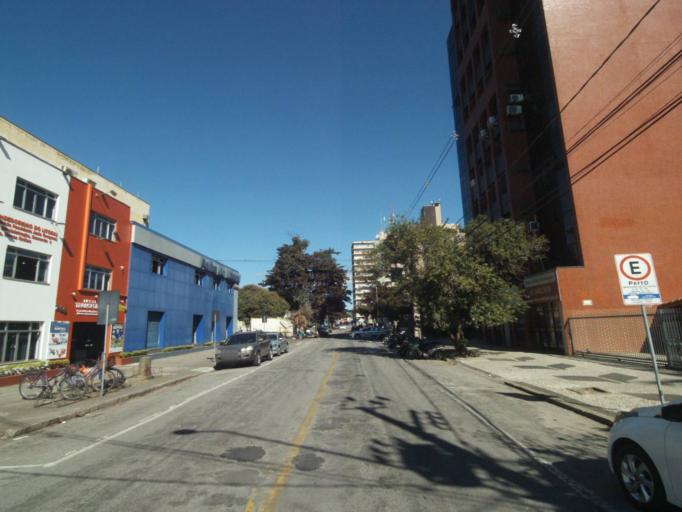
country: BR
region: Parana
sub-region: Paranagua
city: Paranagua
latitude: -25.5163
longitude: -48.5048
